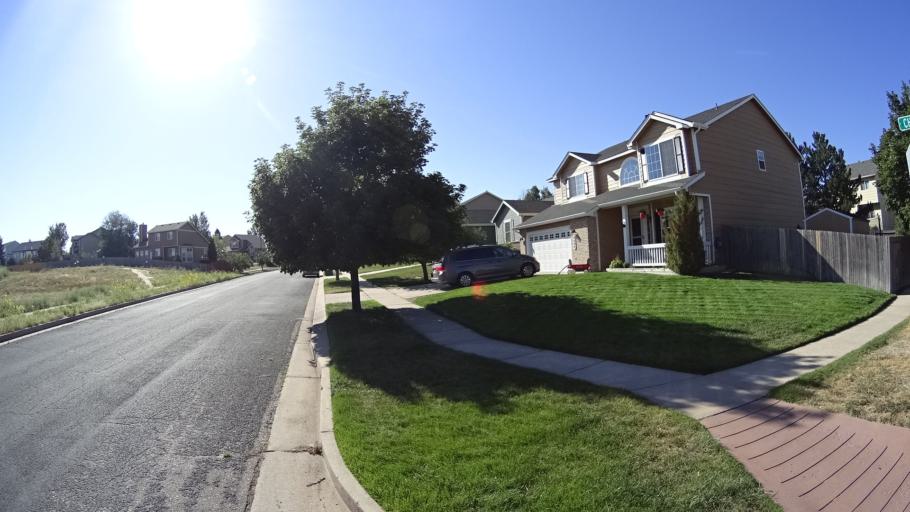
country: US
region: Colorado
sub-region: El Paso County
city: Black Forest
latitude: 38.9620
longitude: -104.7573
